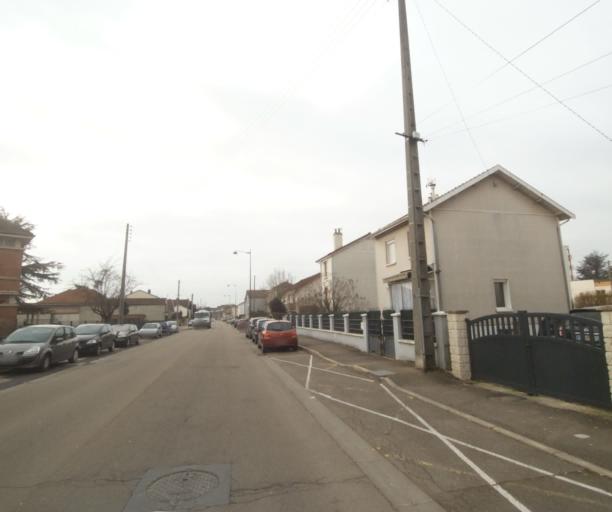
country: FR
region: Champagne-Ardenne
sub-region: Departement de la Haute-Marne
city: Bettancourt-la-Ferree
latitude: 48.6427
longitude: 4.9624
